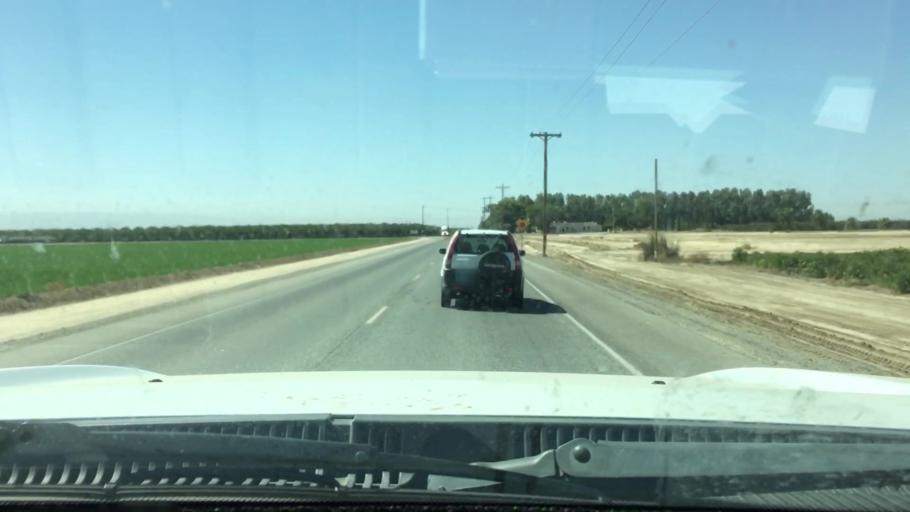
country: US
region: California
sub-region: Kern County
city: Buttonwillow
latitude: 35.5005
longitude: -119.4710
